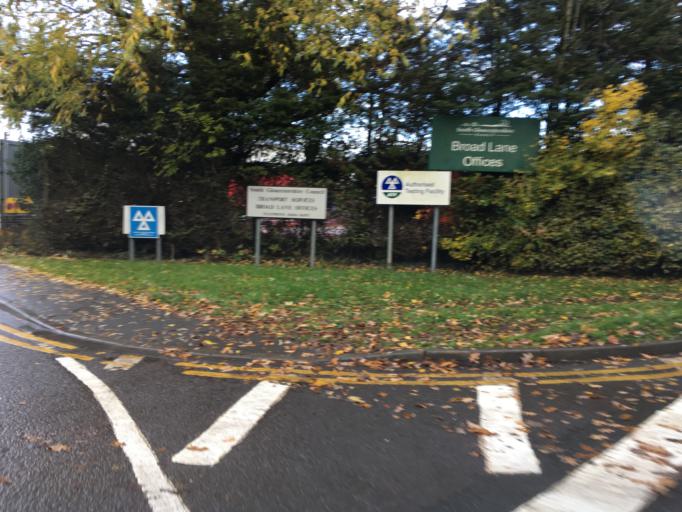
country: GB
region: England
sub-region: South Gloucestershire
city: Yate
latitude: 51.5506
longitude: -2.4309
